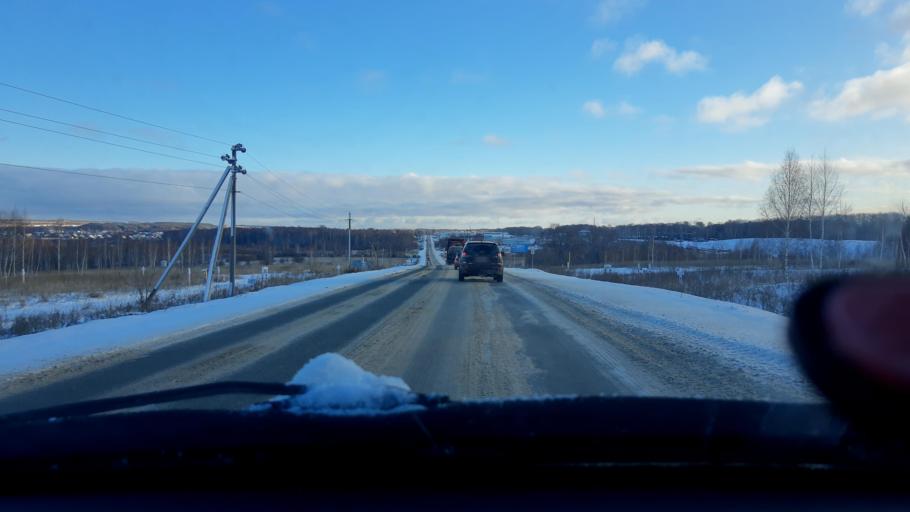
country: RU
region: Bashkortostan
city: Iglino
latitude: 54.8121
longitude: 56.3545
